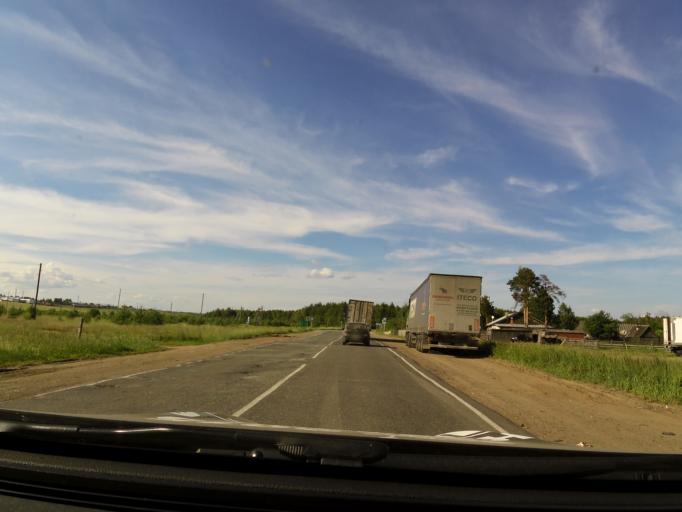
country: RU
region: Kirov
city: Belaya Kholunitsa
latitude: 58.8675
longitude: 50.8432
